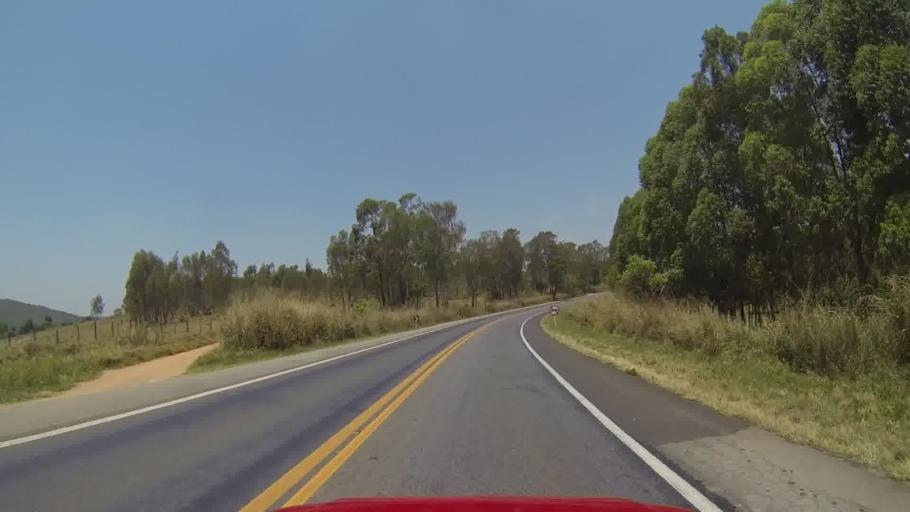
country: BR
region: Minas Gerais
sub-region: Itapecerica
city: Itapecerica
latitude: -20.3054
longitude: -45.2042
